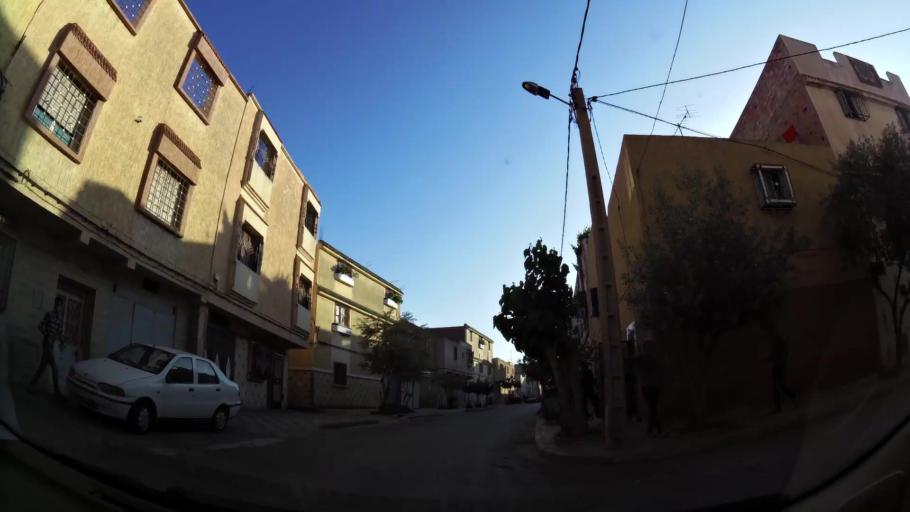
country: MA
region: Oriental
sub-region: Oujda-Angad
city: Oujda
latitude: 34.7007
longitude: -1.9092
